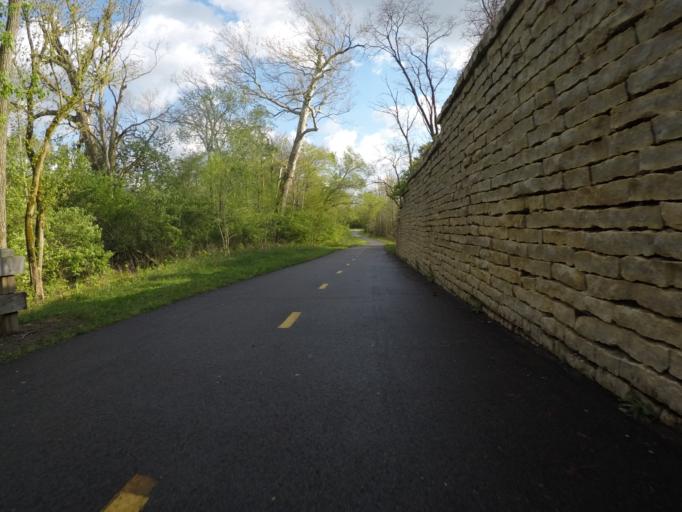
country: US
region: Ohio
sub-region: Franklin County
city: Bexley
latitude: 39.9931
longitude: -82.9380
